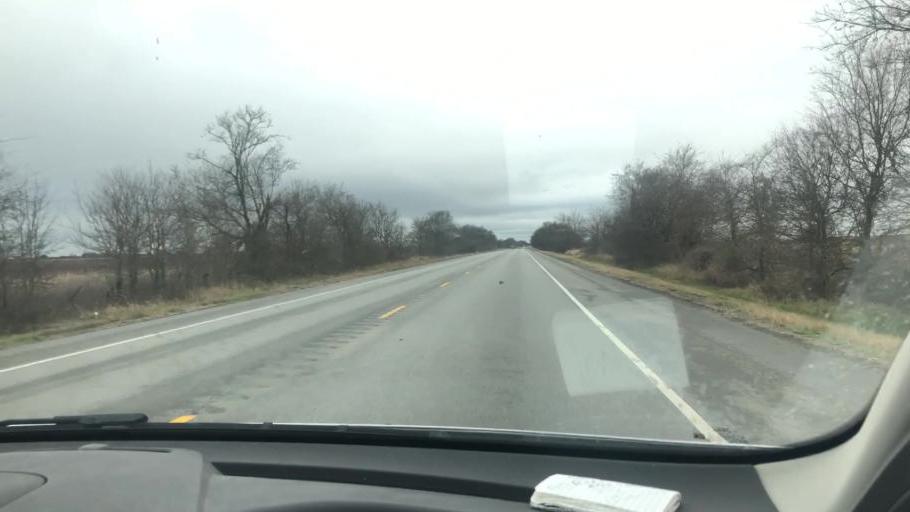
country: US
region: Texas
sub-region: Matagorda County
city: Van Vleck
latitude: 29.1237
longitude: -95.9816
